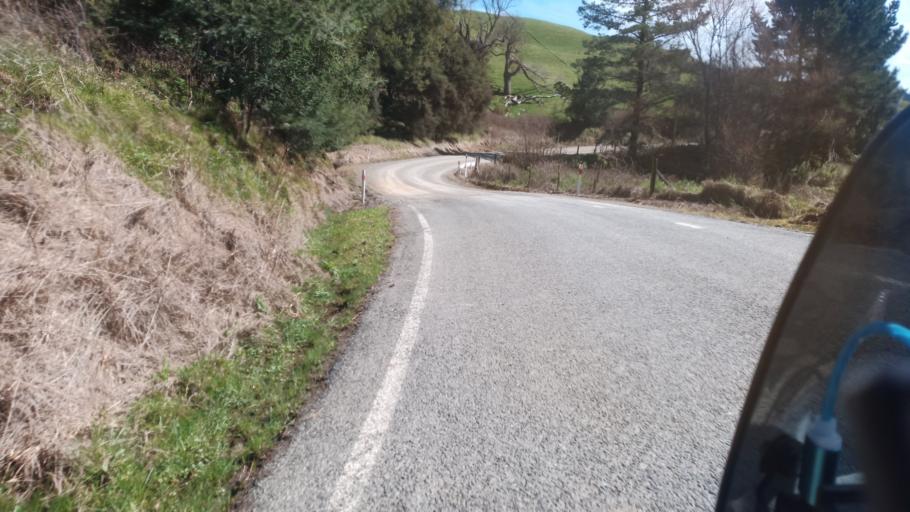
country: NZ
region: Gisborne
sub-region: Gisborne District
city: Gisborne
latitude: -37.9990
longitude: 178.3133
